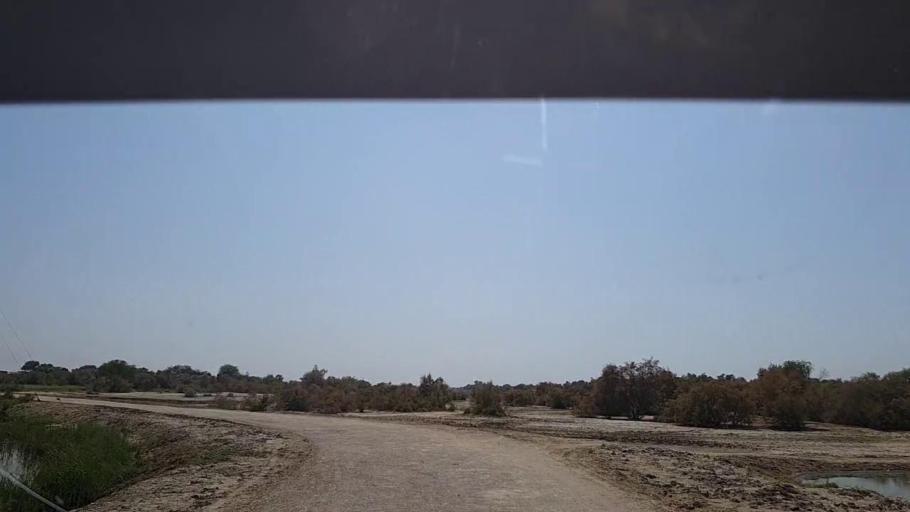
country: PK
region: Sindh
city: Kandhkot
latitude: 28.1857
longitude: 69.1595
